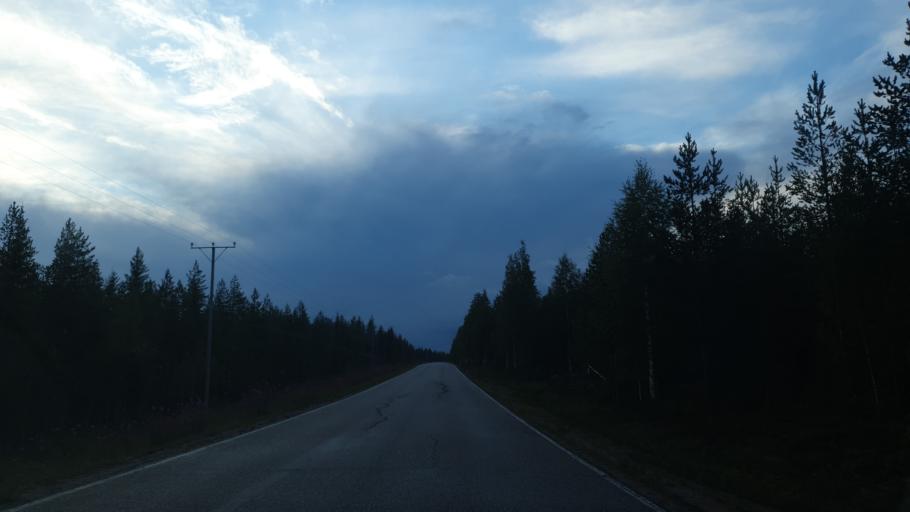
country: FI
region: Kainuu
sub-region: Kehys-Kainuu
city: Kuhmo
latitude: 63.8909
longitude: 29.8183
